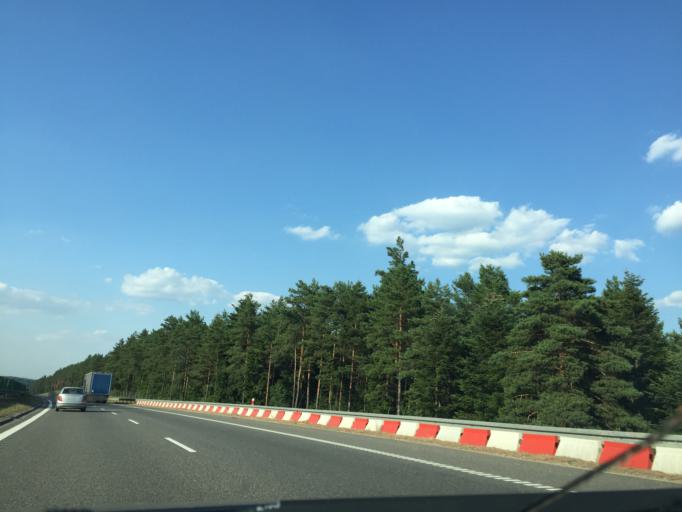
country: PL
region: Swietokrzyskie
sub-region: Powiat skarzyski
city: Laczna
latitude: 51.0138
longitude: 20.8125
